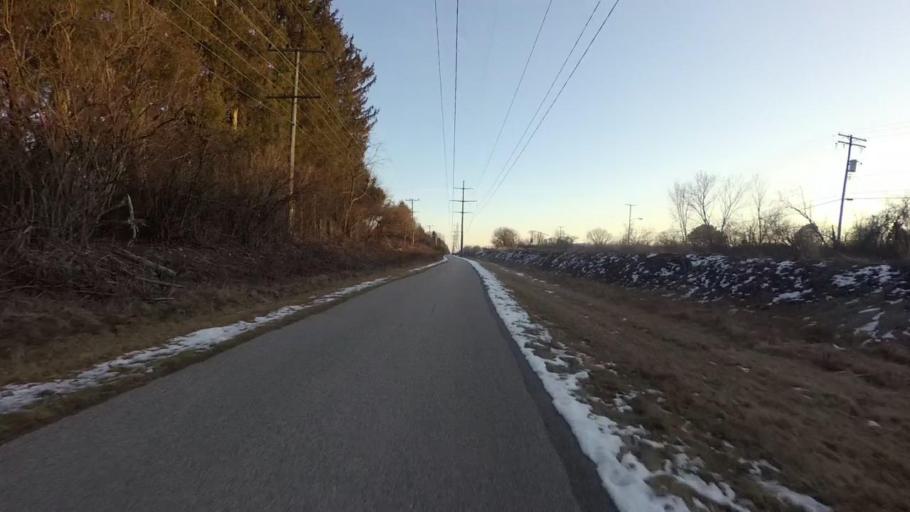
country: US
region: Wisconsin
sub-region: Milwaukee County
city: Brown Deer
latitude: 43.1674
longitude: -87.9626
